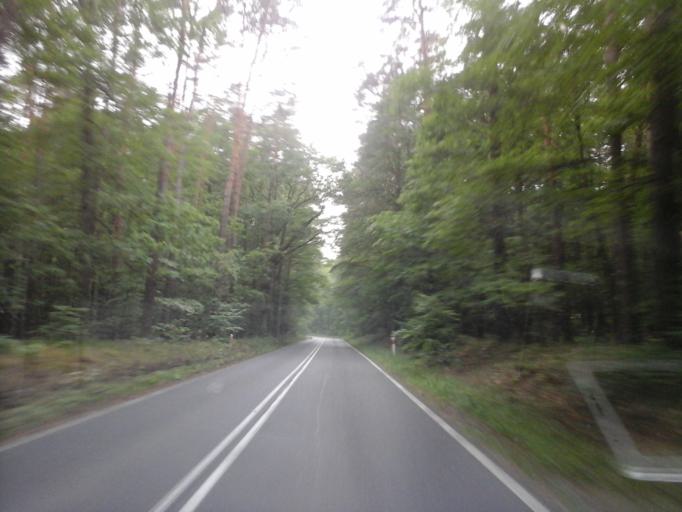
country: PL
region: West Pomeranian Voivodeship
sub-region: Powiat mysliborski
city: Barlinek
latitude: 52.9871
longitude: 15.2372
